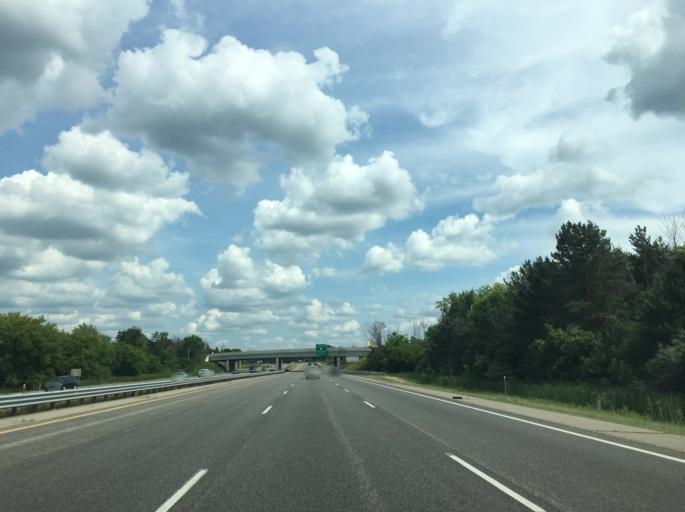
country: US
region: Michigan
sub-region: Genesee County
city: Grand Blanc
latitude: 42.9164
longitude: -83.6755
